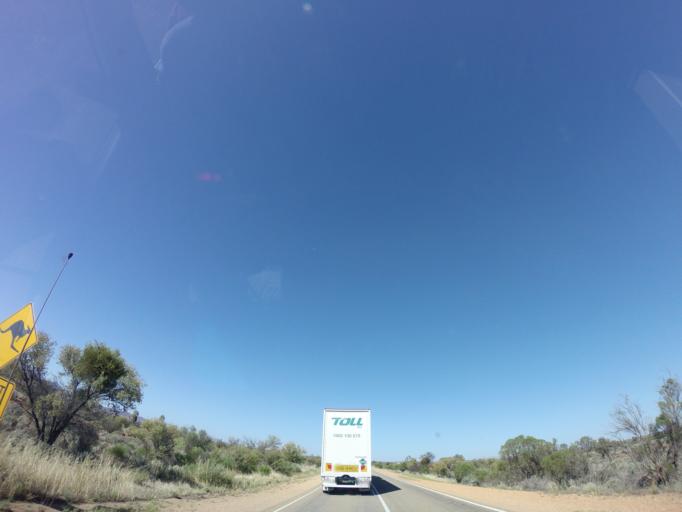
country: AU
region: South Australia
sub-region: Peterborough
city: Peterborough
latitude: -32.5763
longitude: 139.5757
